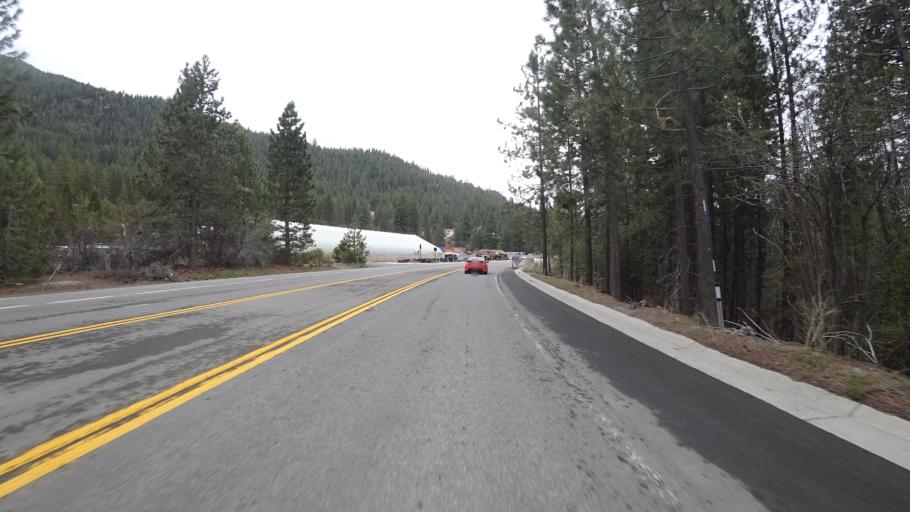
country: US
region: Nevada
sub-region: Washoe County
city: Incline Village
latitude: 39.2385
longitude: -119.9287
